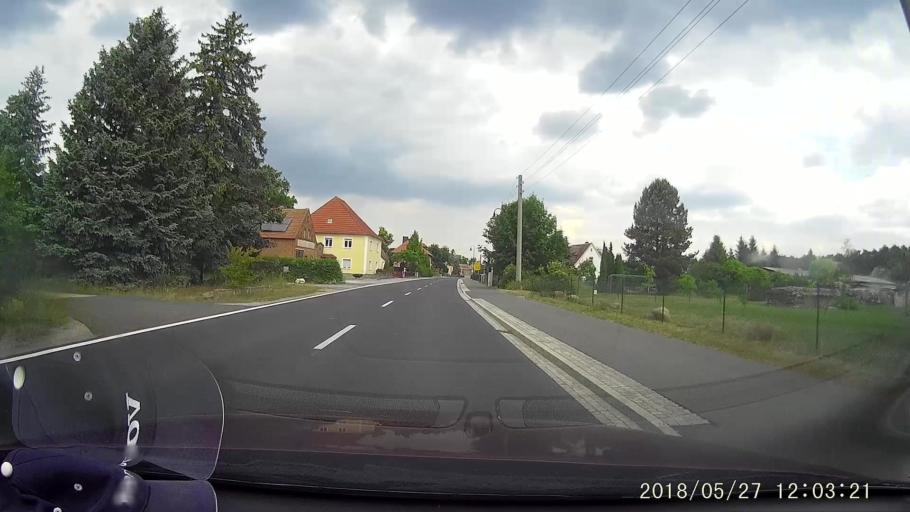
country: DE
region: Saxony
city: Mucka
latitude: 51.3432
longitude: 14.6856
